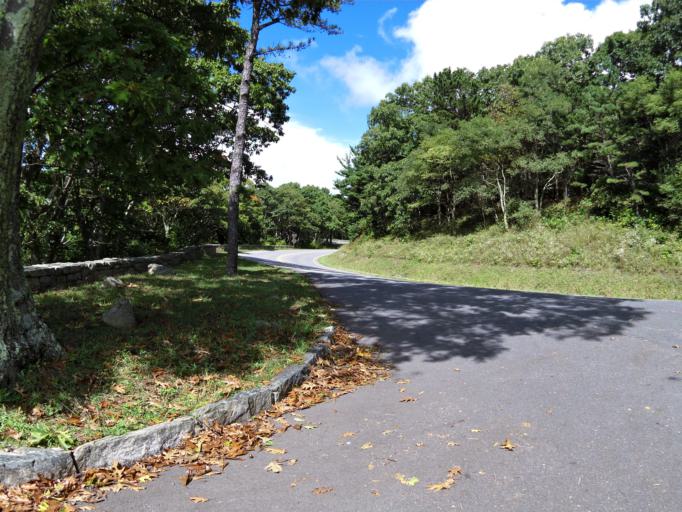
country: US
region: Virginia
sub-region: Page County
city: Luray
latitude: 38.6227
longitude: -78.3232
